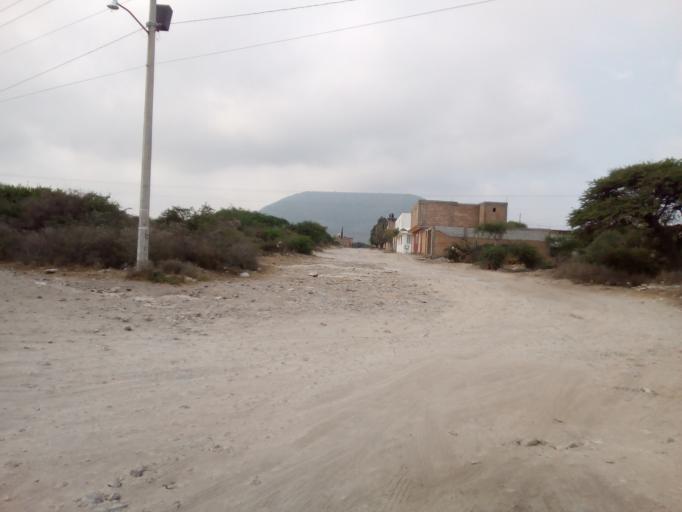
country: MX
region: Guerrero
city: San Luis de la Paz
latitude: 21.2867
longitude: -100.5077
